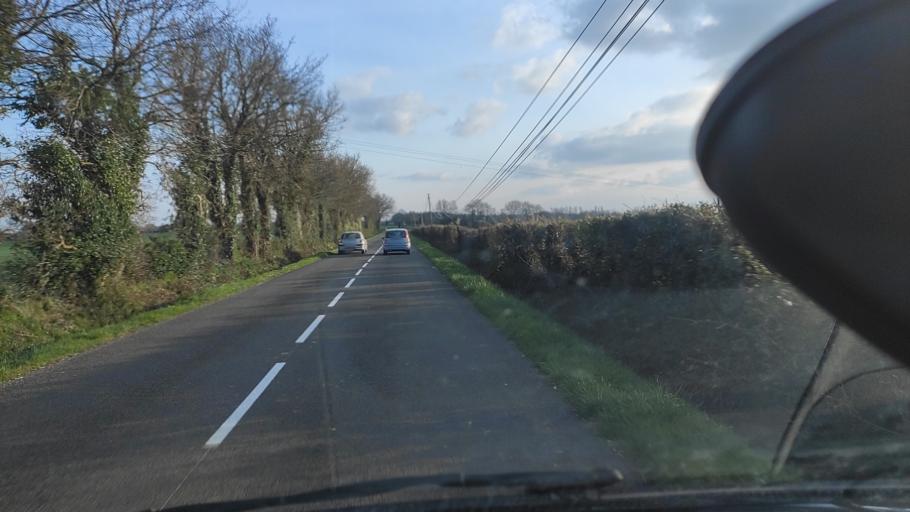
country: FR
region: Pays de la Loire
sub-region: Departement de la Vendee
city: La Chaize-le-Vicomte
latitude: 46.6485
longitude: -1.2976
